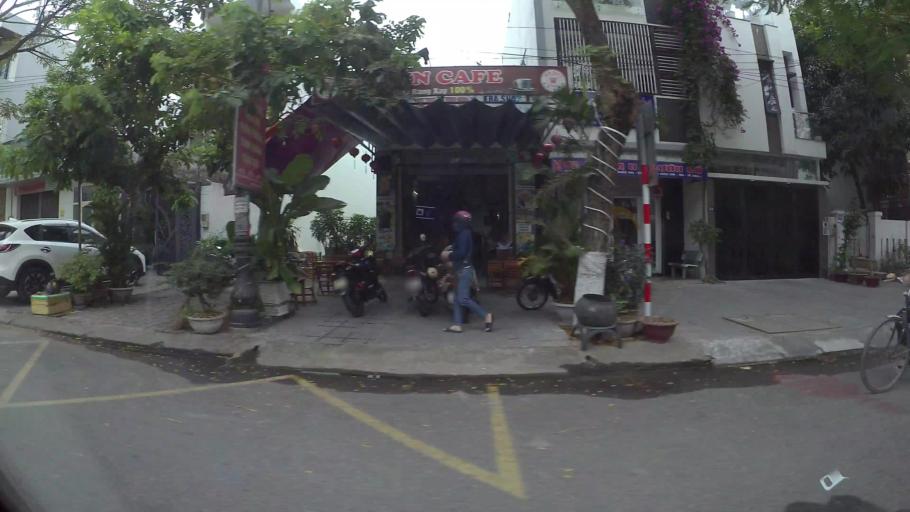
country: VN
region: Da Nang
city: Lien Chieu
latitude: 16.0726
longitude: 108.1730
